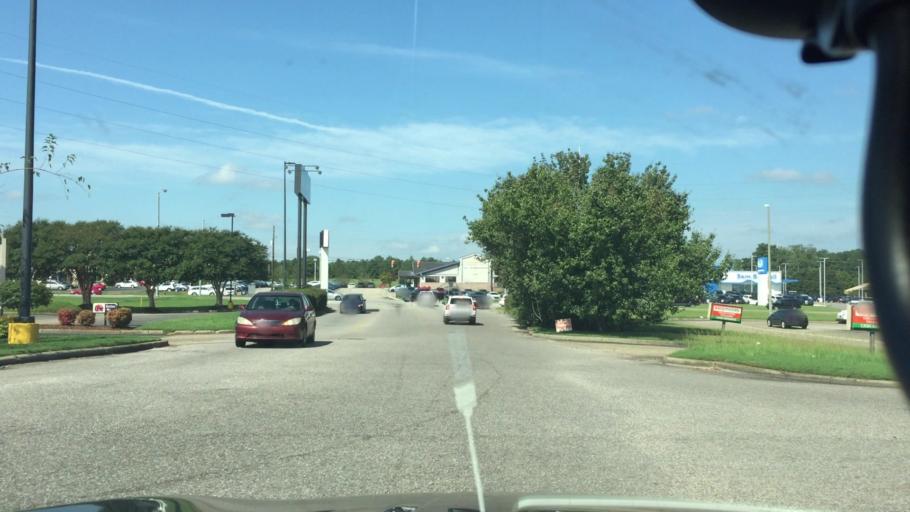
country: US
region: Alabama
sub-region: Coffee County
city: Enterprise
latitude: 31.3158
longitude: -85.8289
